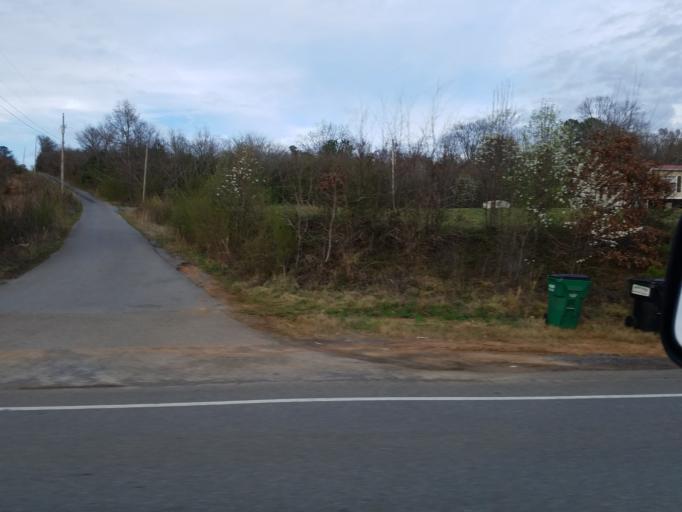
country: US
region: Georgia
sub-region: Gordon County
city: Calhoun
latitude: 34.4569
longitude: -84.9049
